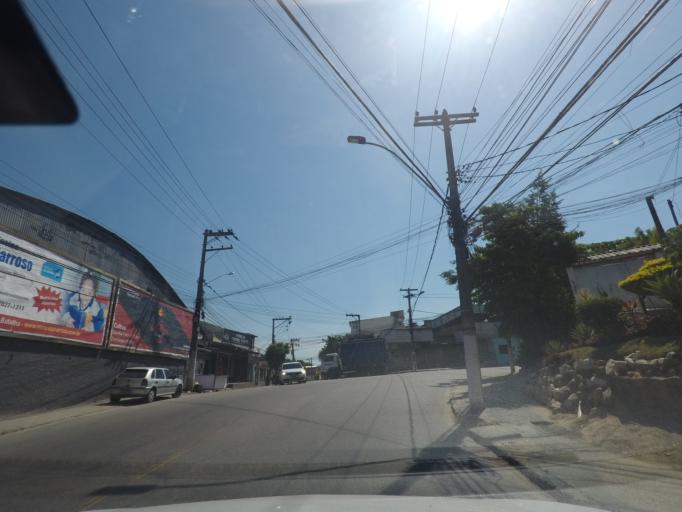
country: BR
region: Rio de Janeiro
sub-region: Niteroi
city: Niteroi
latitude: -22.9061
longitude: -43.0699
